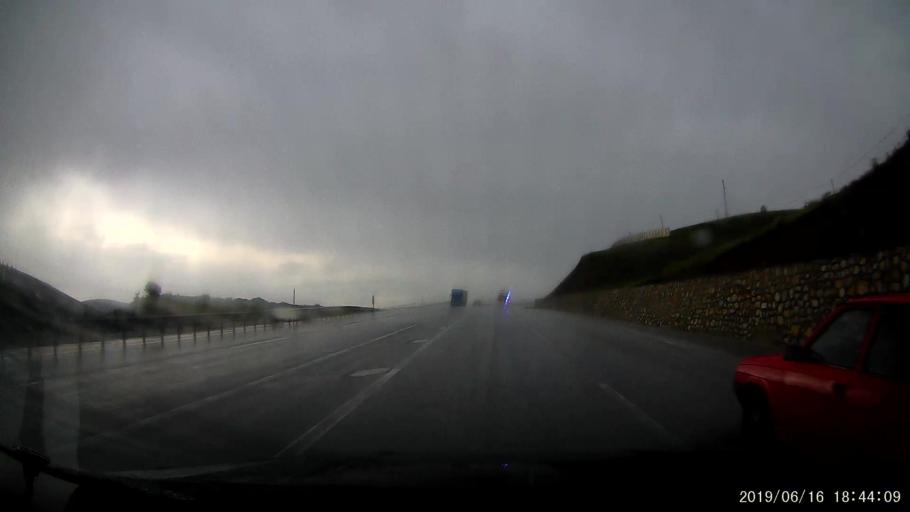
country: TR
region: Erzincan
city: Doganbeyli
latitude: 39.8702
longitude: 39.0784
